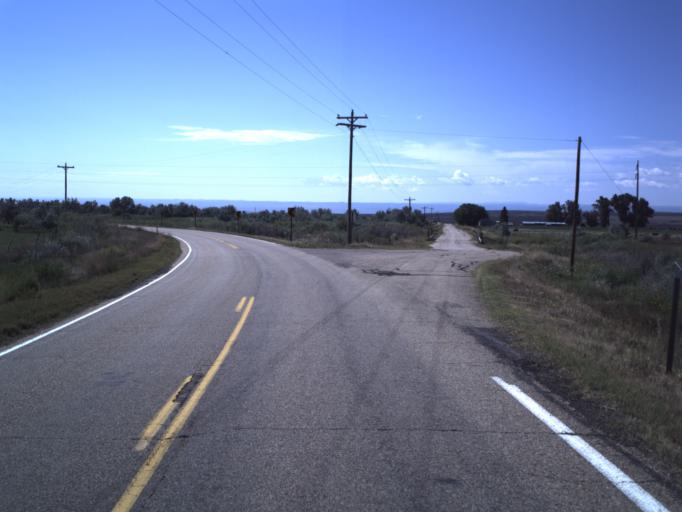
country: US
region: Utah
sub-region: Duchesne County
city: Duchesne
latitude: 40.3358
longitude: -110.2752
